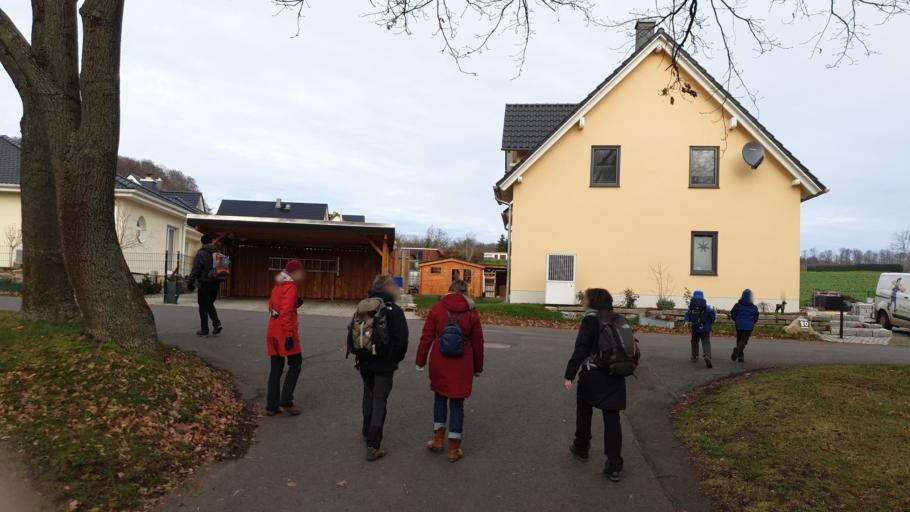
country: DE
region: Saxony
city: Hohburg
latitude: 51.4144
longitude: 12.8047
